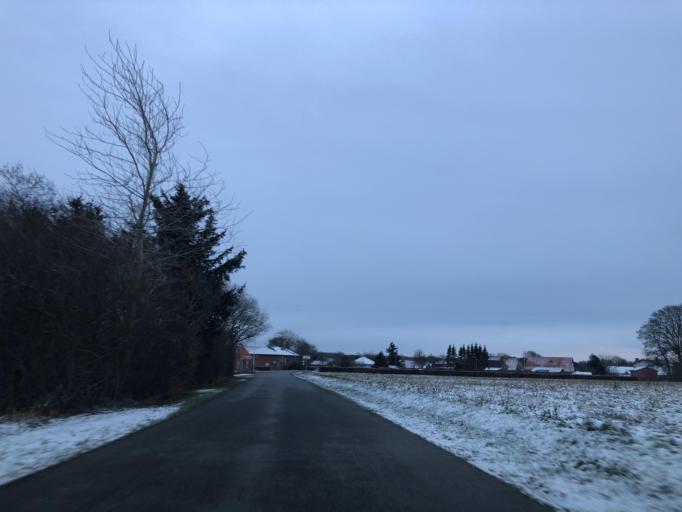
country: DK
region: Central Jutland
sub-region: Holstebro Kommune
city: Ulfborg
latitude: 56.1451
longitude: 8.4295
